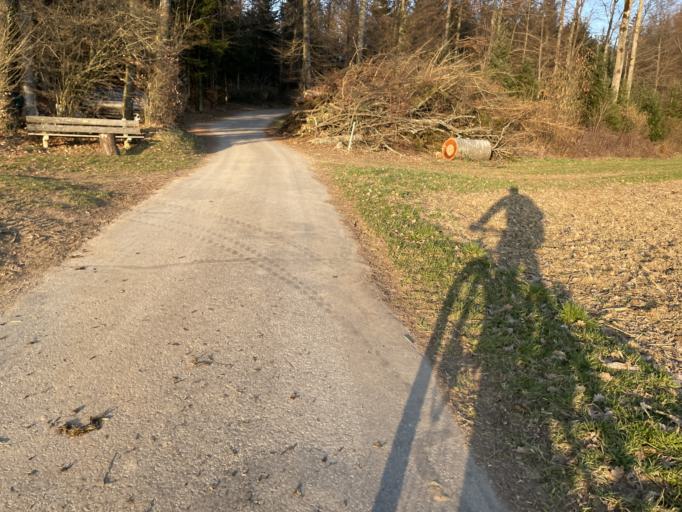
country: CH
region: Bern
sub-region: Bern-Mittelland District
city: Worb
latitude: 46.9169
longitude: 7.5552
